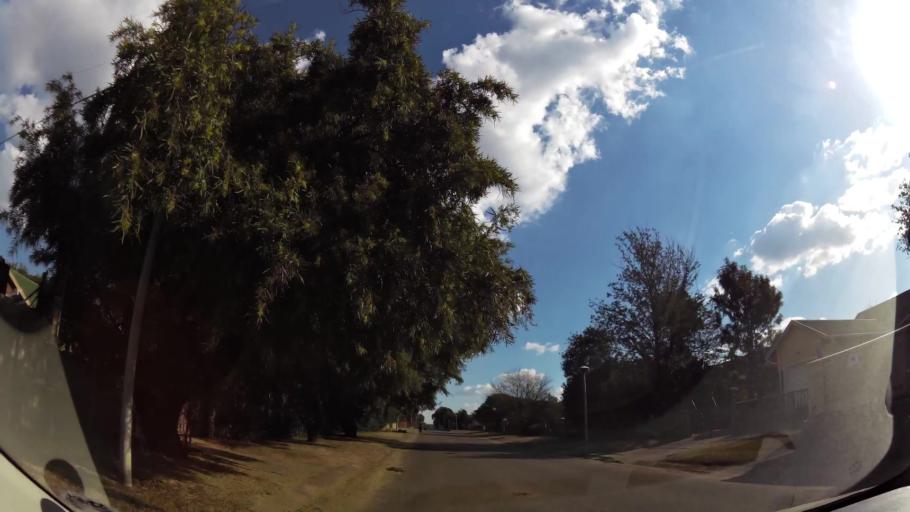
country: ZA
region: Mpumalanga
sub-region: Nkangala District Municipality
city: Witbank
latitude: -25.9159
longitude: 29.2284
